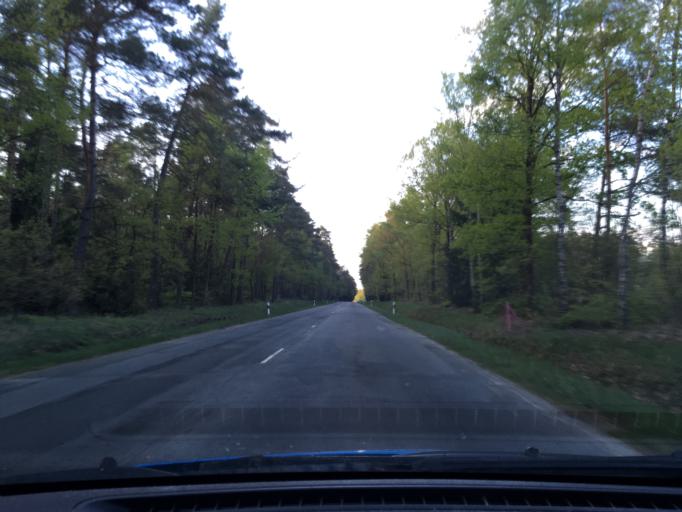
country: DE
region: Lower Saxony
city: Wietzendorf
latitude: 52.9752
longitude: 9.9823
